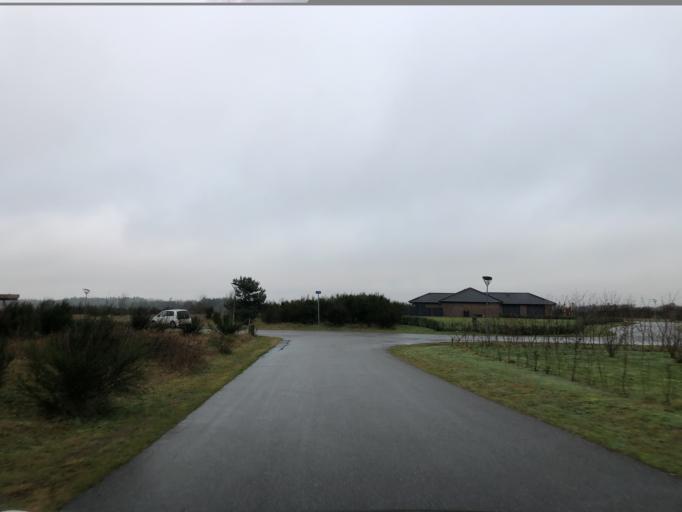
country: DK
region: Central Jutland
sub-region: Holstebro Kommune
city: Ulfborg
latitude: 56.1986
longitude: 8.3048
